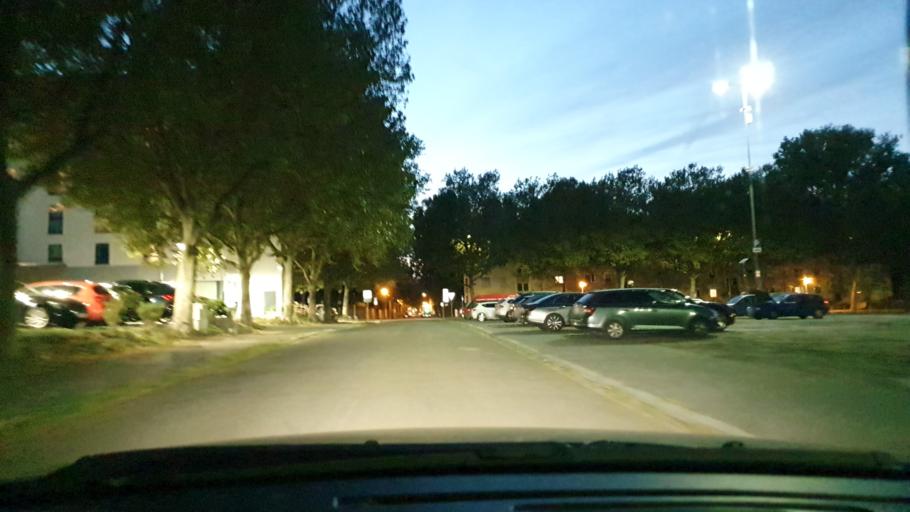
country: DE
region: Rheinland-Pfalz
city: Kaiserslautern
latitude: 49.4424
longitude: 7.7853
